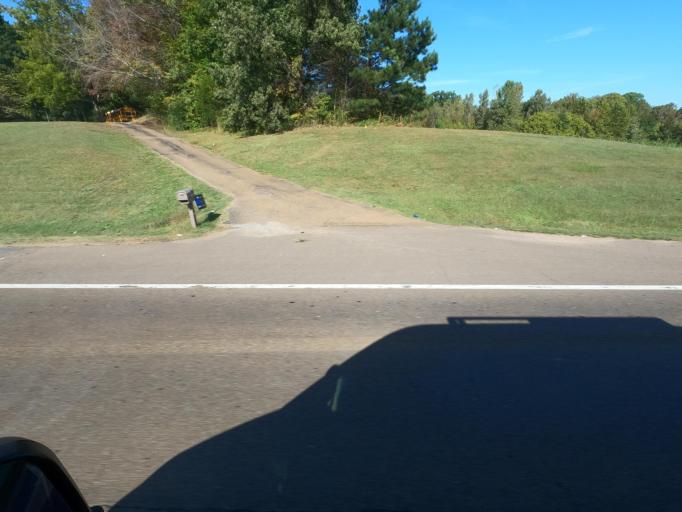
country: US
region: Tennessee
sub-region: Tipton County
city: Munford
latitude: 35.4188
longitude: -89.8224
